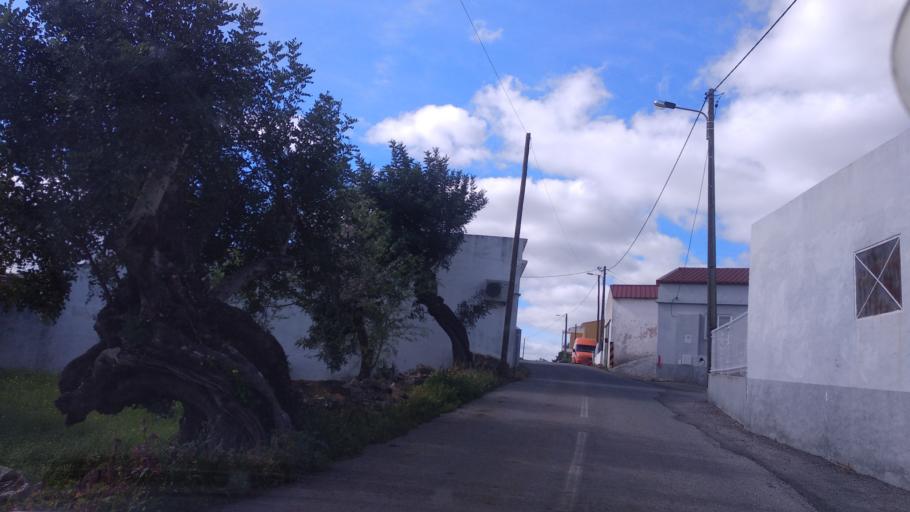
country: PT
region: Faro
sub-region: Sao Bras de Alportel
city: Sao Bras de Alportel
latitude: 37.1493
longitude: -7.9019
